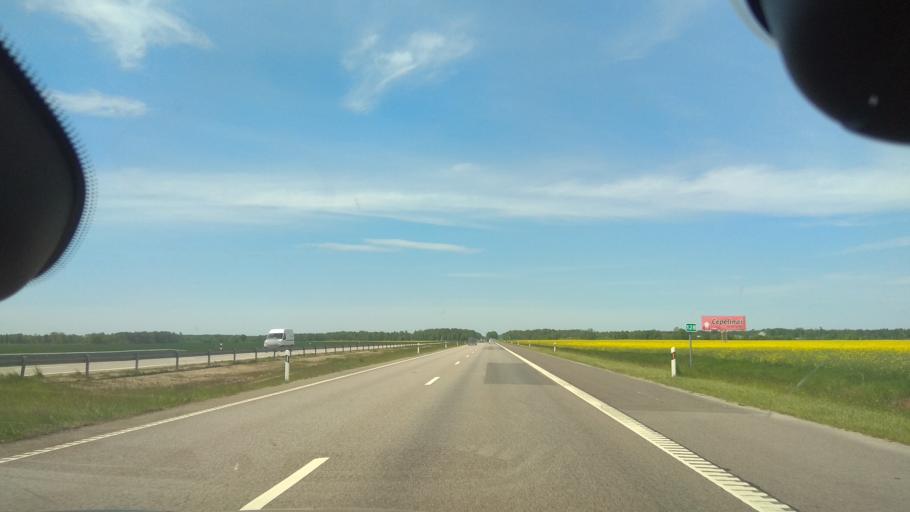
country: LT
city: Vilkija
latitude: 55.1438
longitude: 23.7160
